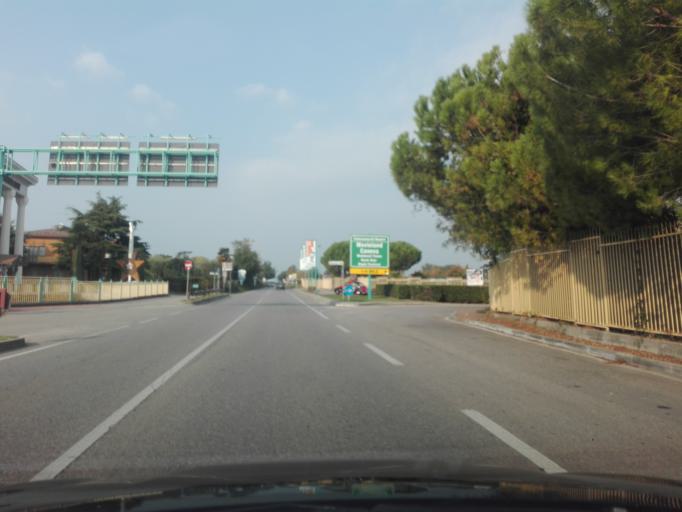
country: IT
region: Veneto
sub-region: Provincia di Verona
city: Cola
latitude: 45.4784
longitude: 10.7281
